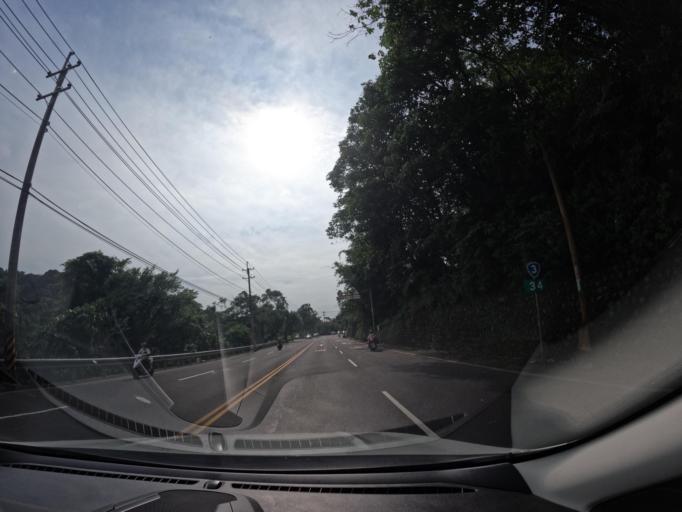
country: TW
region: Taiwan
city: Daxi
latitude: 24.8938
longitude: 121.3064
